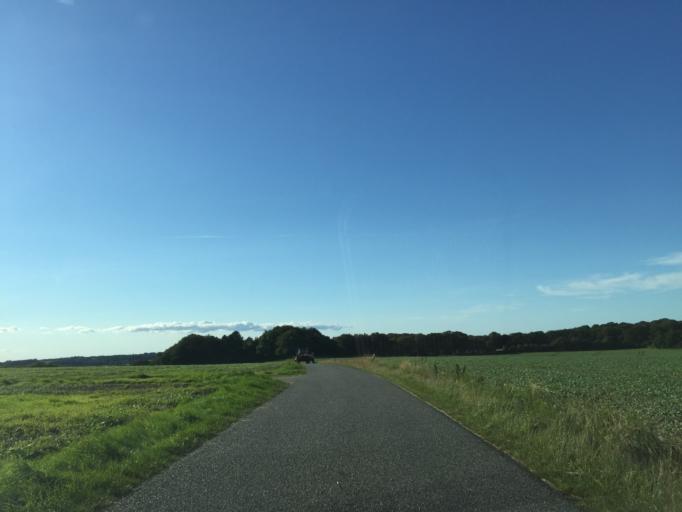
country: DK
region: Central Jutland
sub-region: Silkeborg Kommune
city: Svejbaek
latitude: 56.2422
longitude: 9.6960
